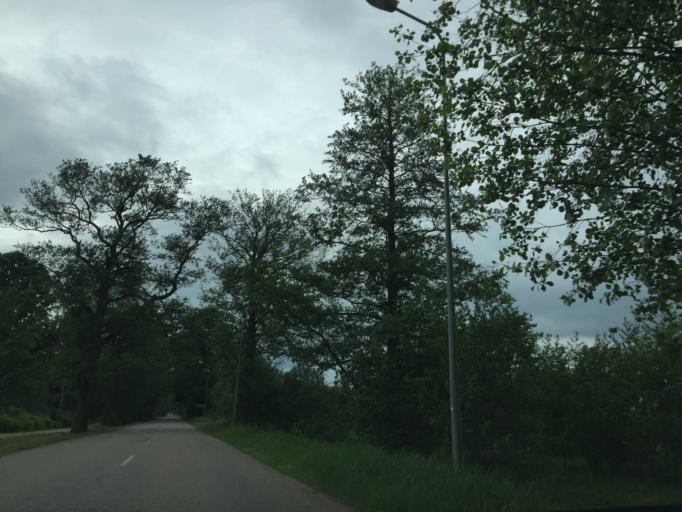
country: LV
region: Preilu Rajons
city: Preili
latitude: 56.0725
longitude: 26.7422
